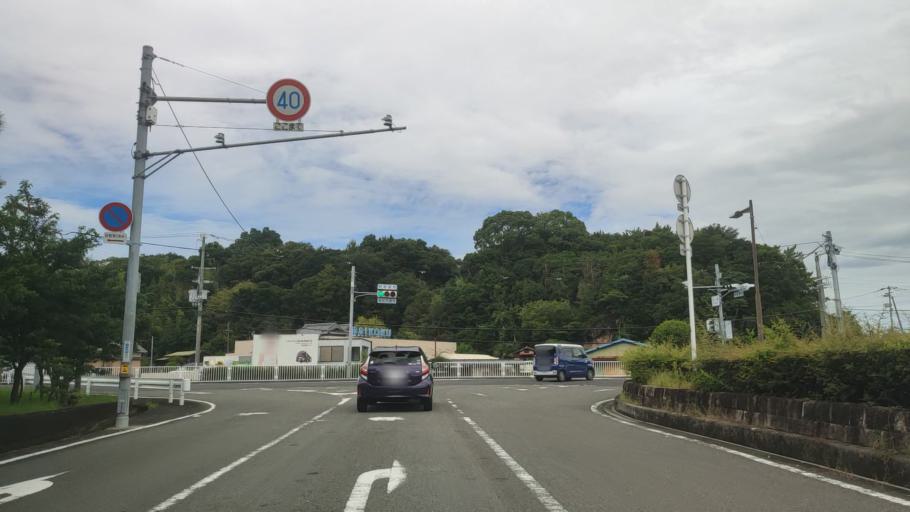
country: JP
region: Wakayama
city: Tanabe
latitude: 33.6923
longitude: 135.3864
